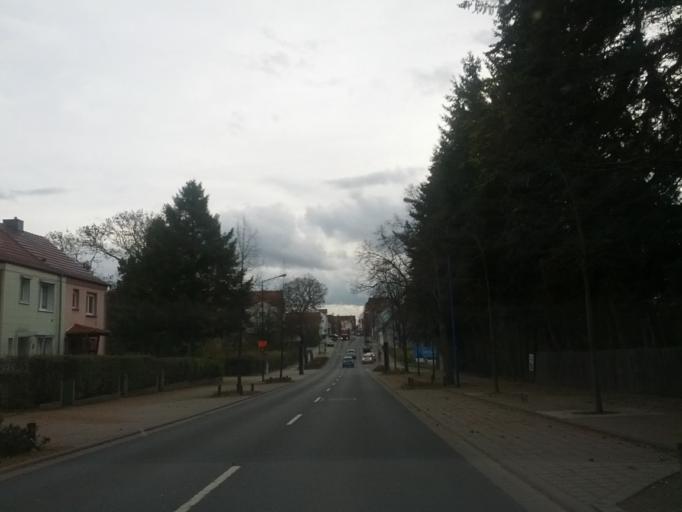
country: DE
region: Thuringia
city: Gotha
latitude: 50.9622
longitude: 10.7071
